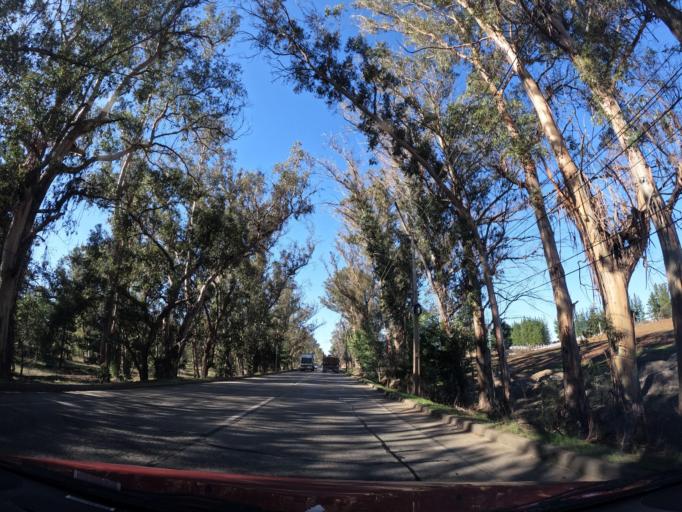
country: CL
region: Maule
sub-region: Provincia de Cauquenes
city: Cauquenes
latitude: -35.9578
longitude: -72.2844
